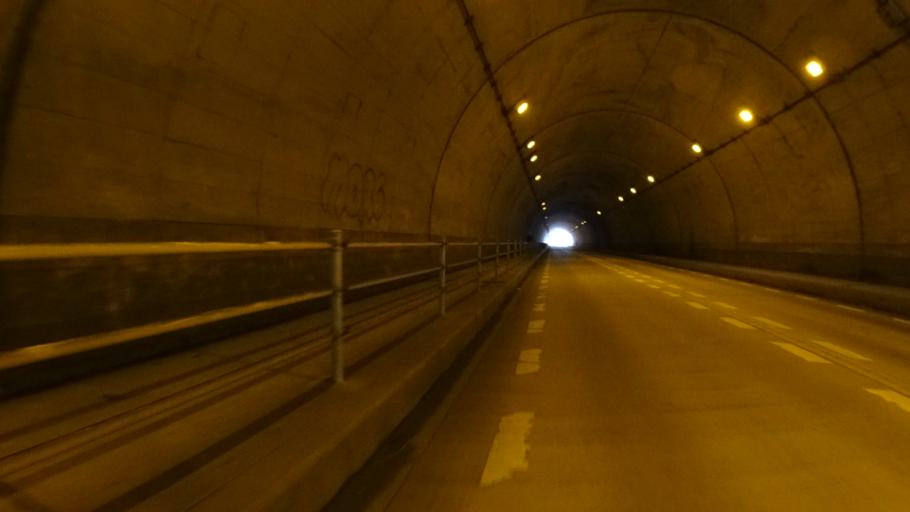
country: JP
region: Kanagawa
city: Yokosuka
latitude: 35.2325
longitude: 139.7223
